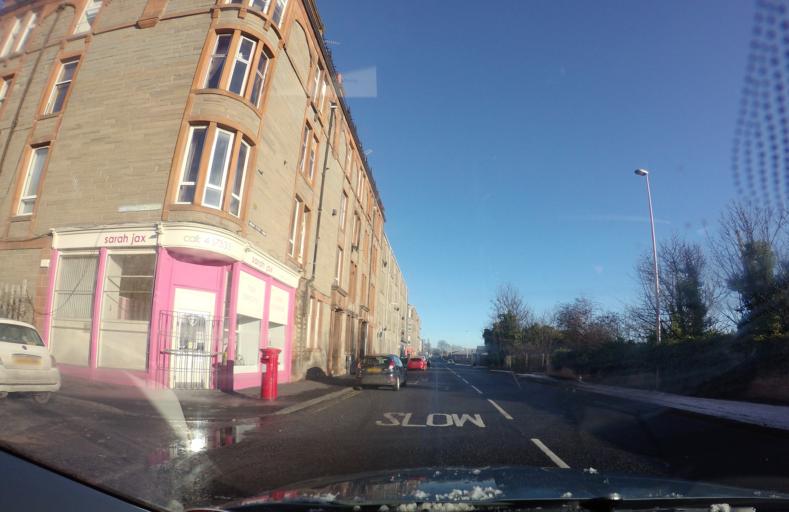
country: GB
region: Scotland
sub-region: Dundee City
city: Dundee
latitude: 56.4665
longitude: -2.9525
